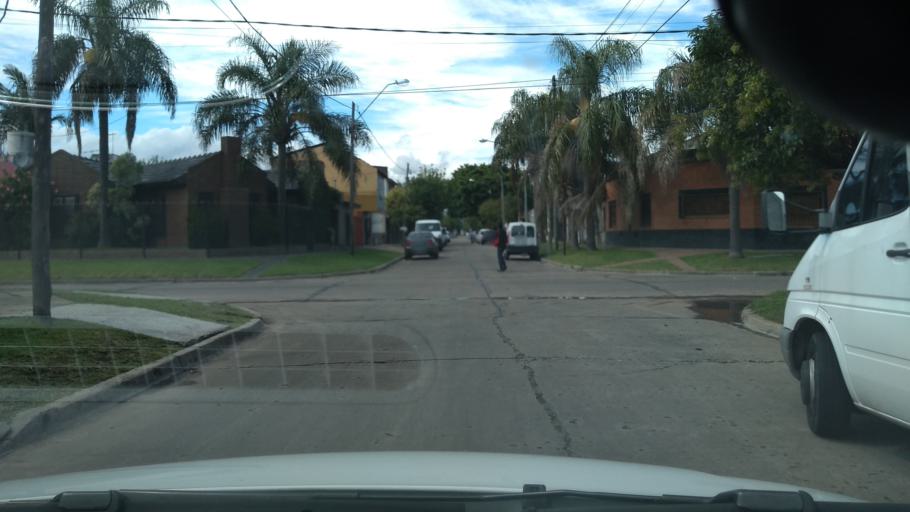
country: AR
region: Buenos Aires
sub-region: Partido de Moron
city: Moron
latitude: -34.6643
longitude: -58.6091
